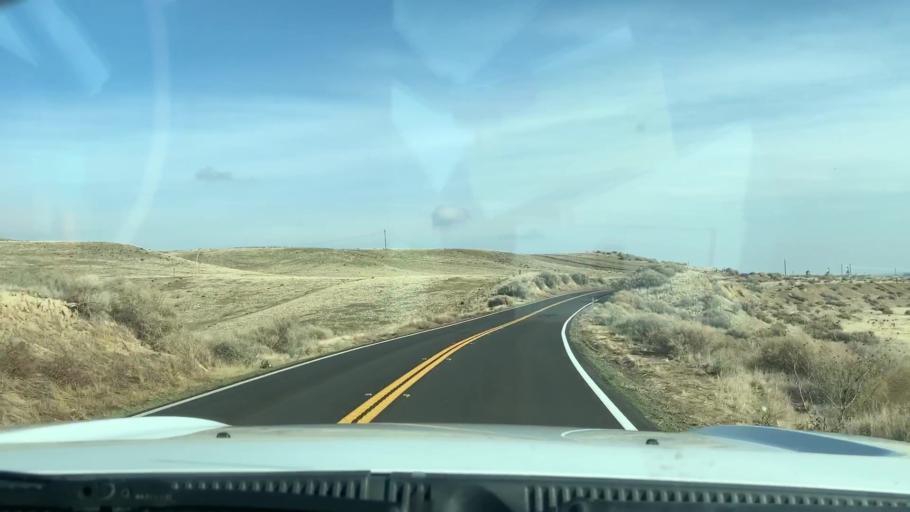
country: US
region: California
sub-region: Fresno County
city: Coalinga
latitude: 36.1150
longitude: -120.3825
